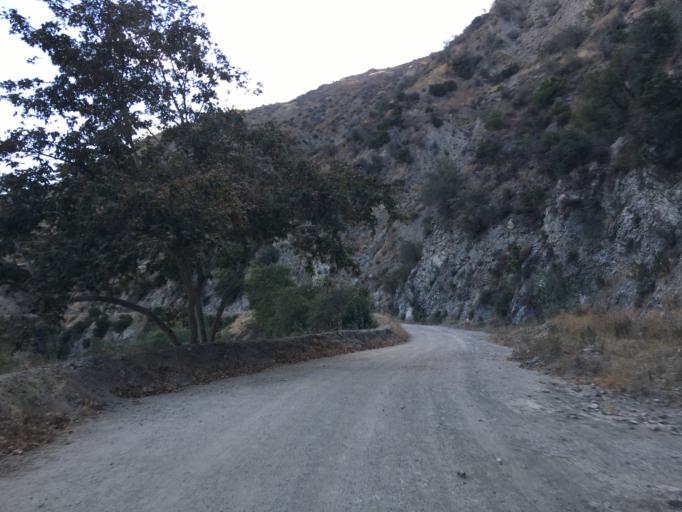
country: US
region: California
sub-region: Los Angeles County
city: Azusa
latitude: 34.1611
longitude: -117.8895
